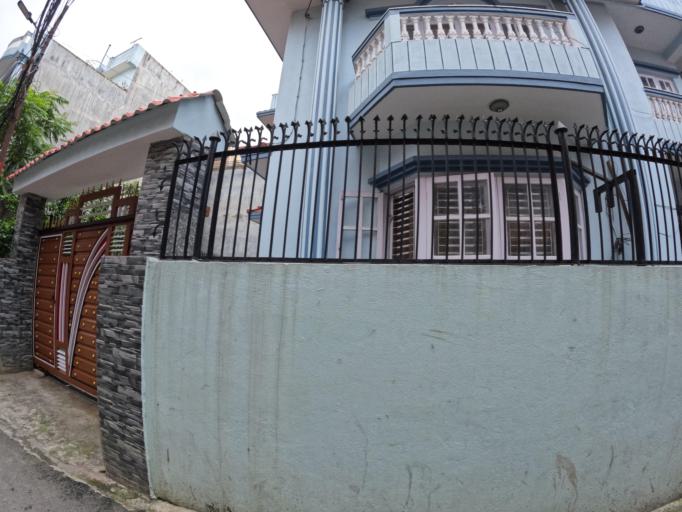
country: NP
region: Central Region
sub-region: Bagmati Zone
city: Kathmandu
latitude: 27.7373
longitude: 85.3161
